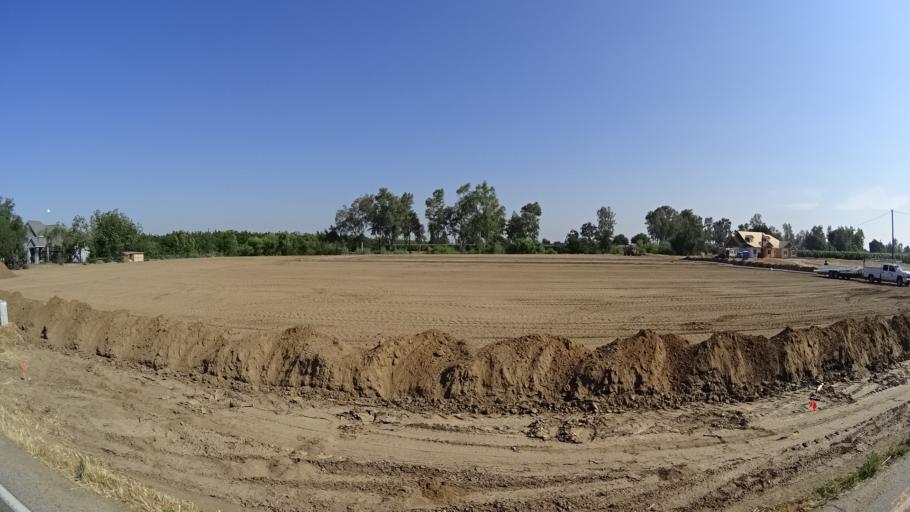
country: US
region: California
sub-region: Fresno County
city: Kingsburg
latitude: 36.4813
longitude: -119.5633
